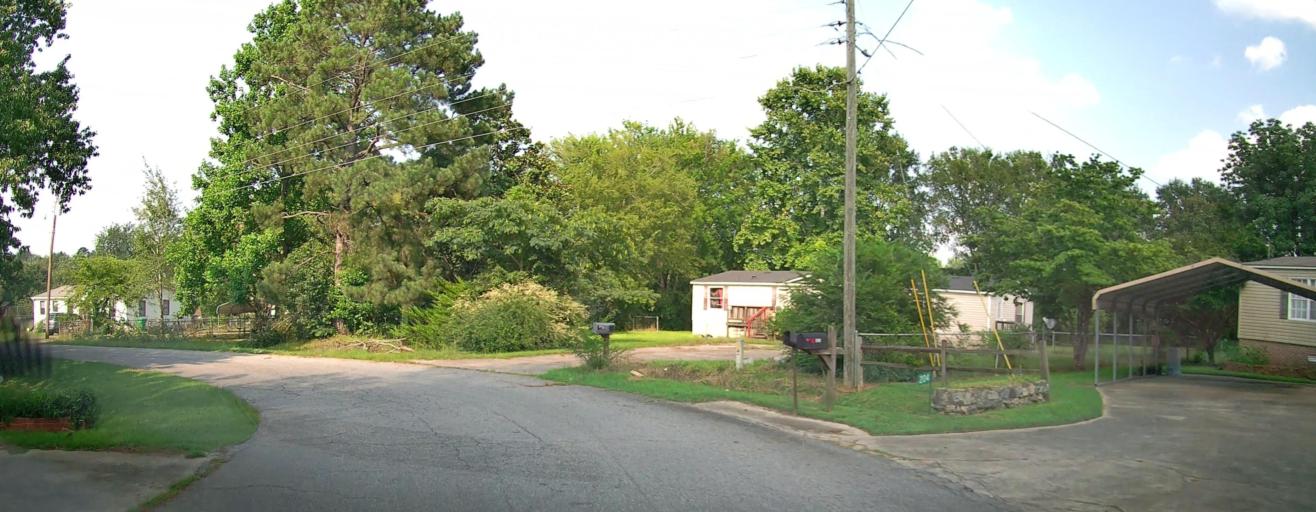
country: US
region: Georgia
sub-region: Houston County
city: Centerville
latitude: 32.6442
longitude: -83.6834
